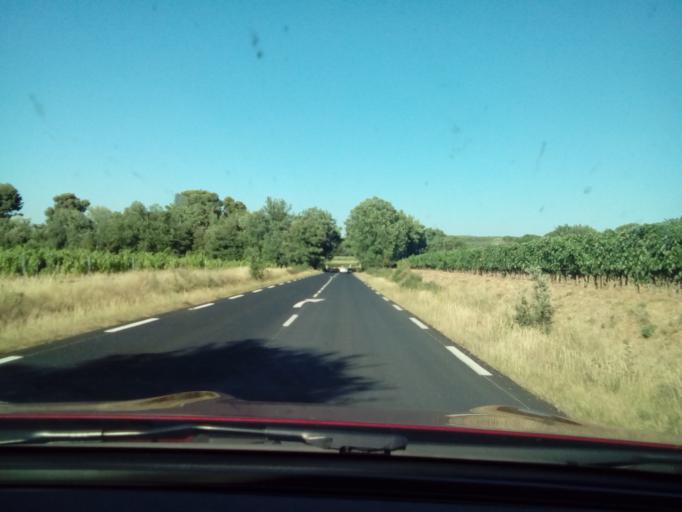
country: FR
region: Provence-Alpes-Cote d'Azur
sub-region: Departement du Var
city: Pourrieres
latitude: 43.4663
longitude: 5.7326
